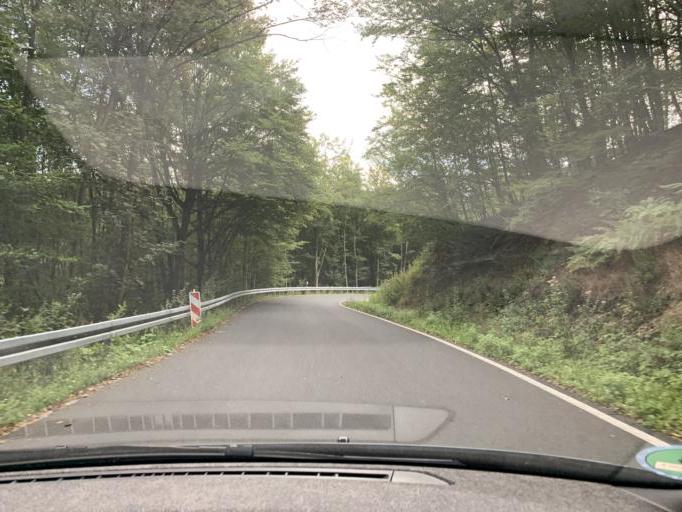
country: DE
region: North Rhine-Westphalia
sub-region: Regierungsbezirk Koln
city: Hurtgenwald
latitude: 50.6719
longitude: 6.3605
